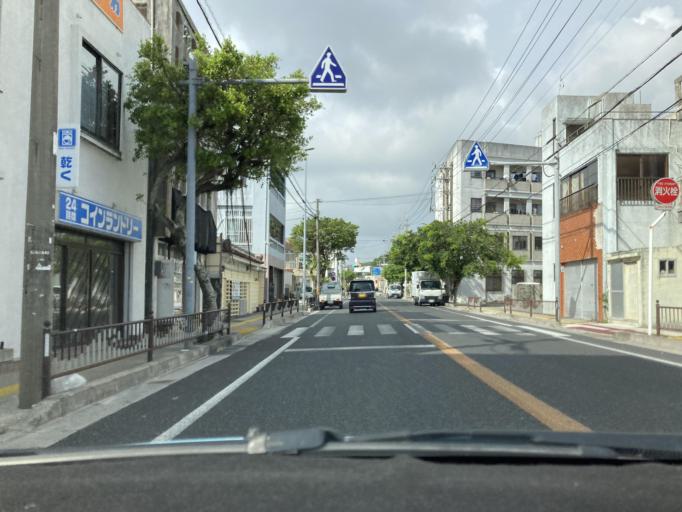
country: JP
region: Okinawa
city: Itoman
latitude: 26.1307
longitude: 127.6699
